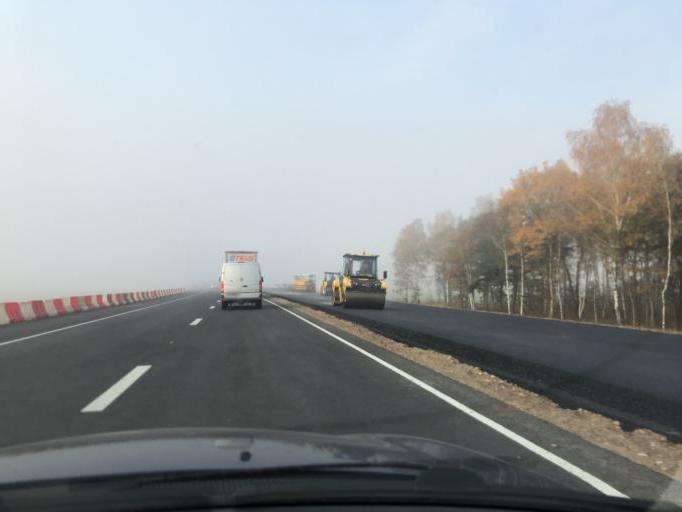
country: BY
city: Berezovka
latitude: 53.8418
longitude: 25.4832
